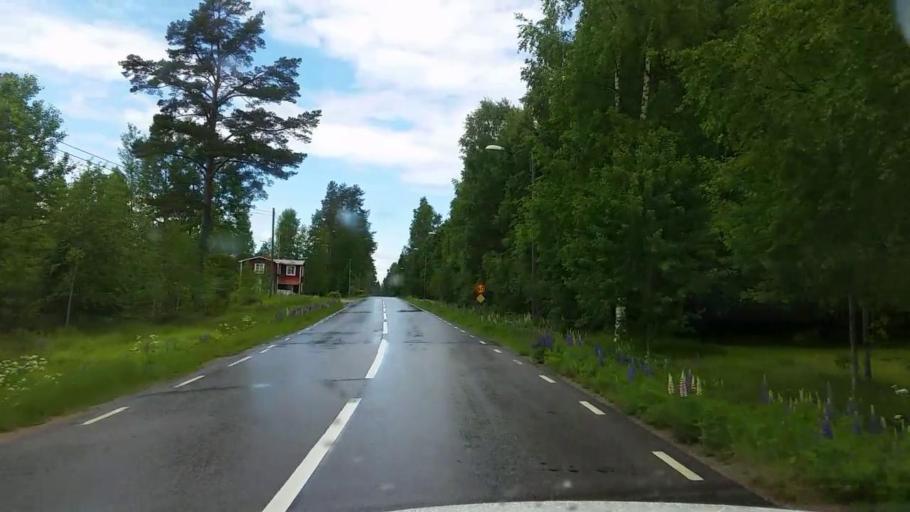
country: SE
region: Gaevleborg
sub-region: Sandvikens Kommun
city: Jarbo
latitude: 60.8366
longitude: 16.4927
